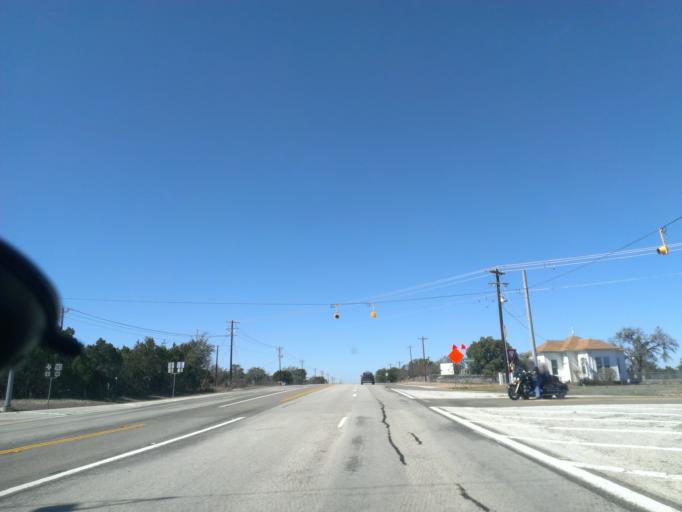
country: US
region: Texas
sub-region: Lampasas County
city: Kempner
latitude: 30.9342
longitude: -98.0139
